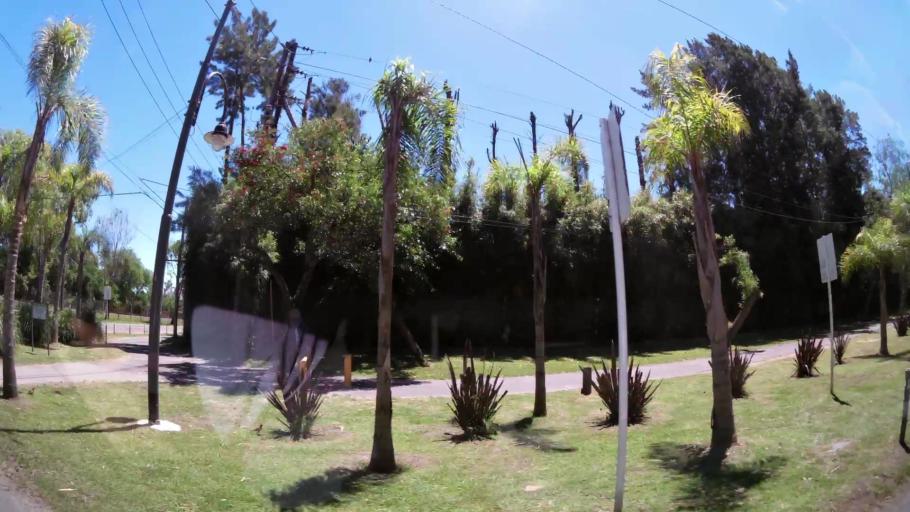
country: AR
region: Buenos Aires
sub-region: Partido de Tigre
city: Tigre
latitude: -34.4438
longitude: -58.5413
